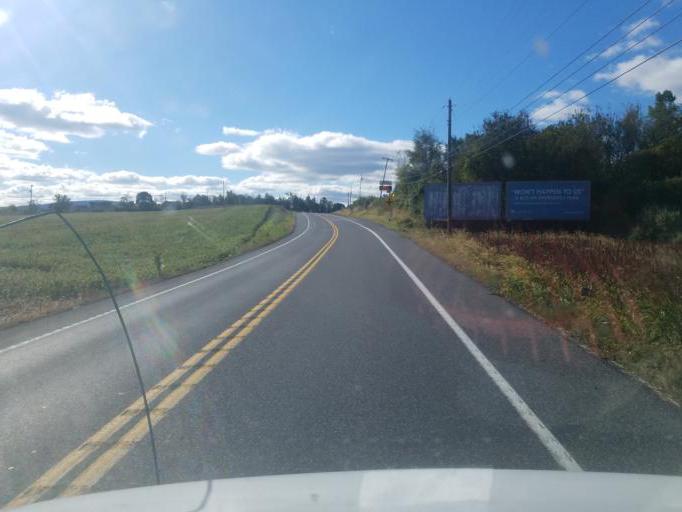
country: US
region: Pennsylvania
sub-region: Franklin County
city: Waynesboro
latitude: 39.7732
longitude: -77.5690
